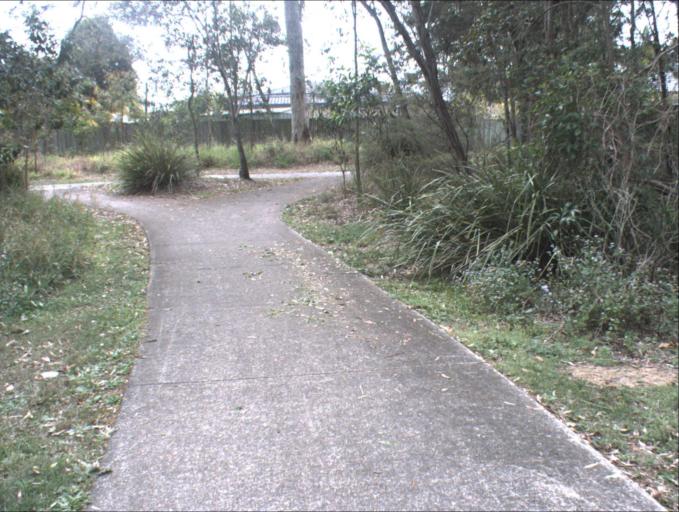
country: AU
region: Queensland
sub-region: Logan
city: Park Ridge South
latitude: -27.6883
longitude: 153.0590
